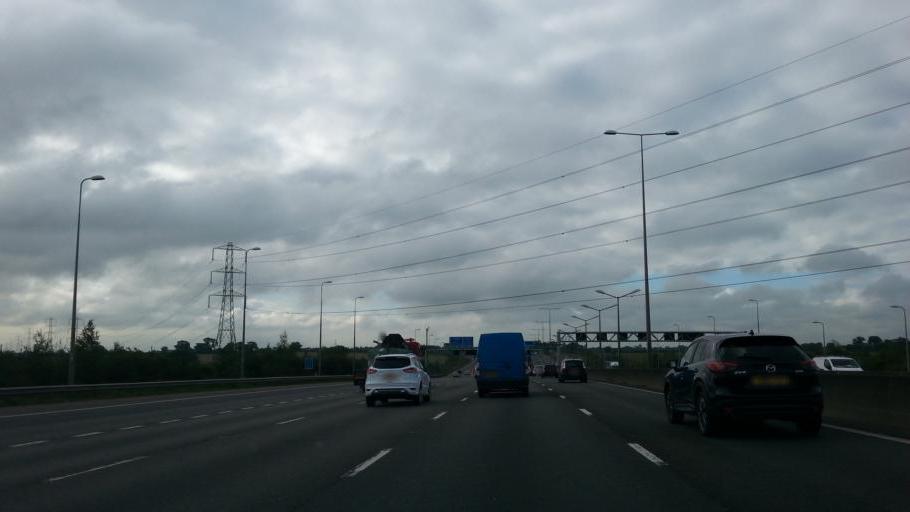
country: GB
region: England
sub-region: Hertfordshire
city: Redbourn
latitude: 51.7686
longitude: -0.4147
